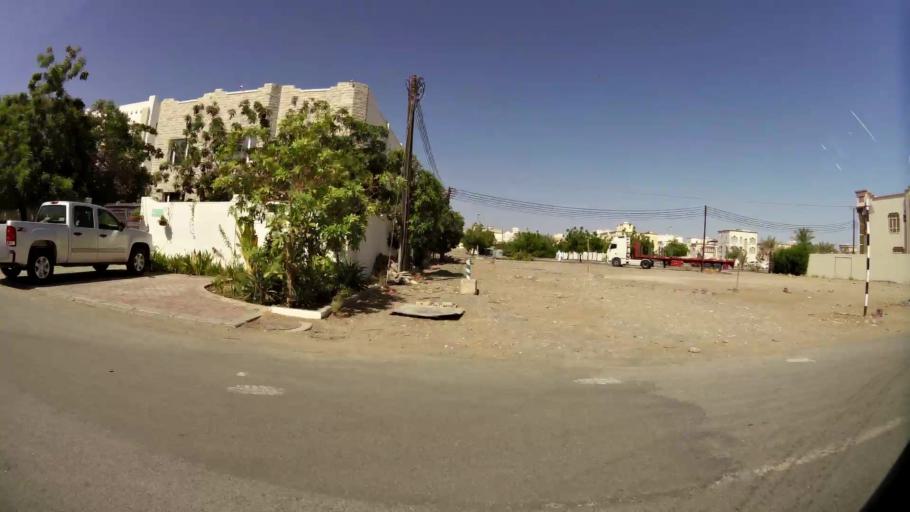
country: OM
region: Muhafazat Masqat
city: As Sib al Jadidah
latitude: 23.6058
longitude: 58.2375
